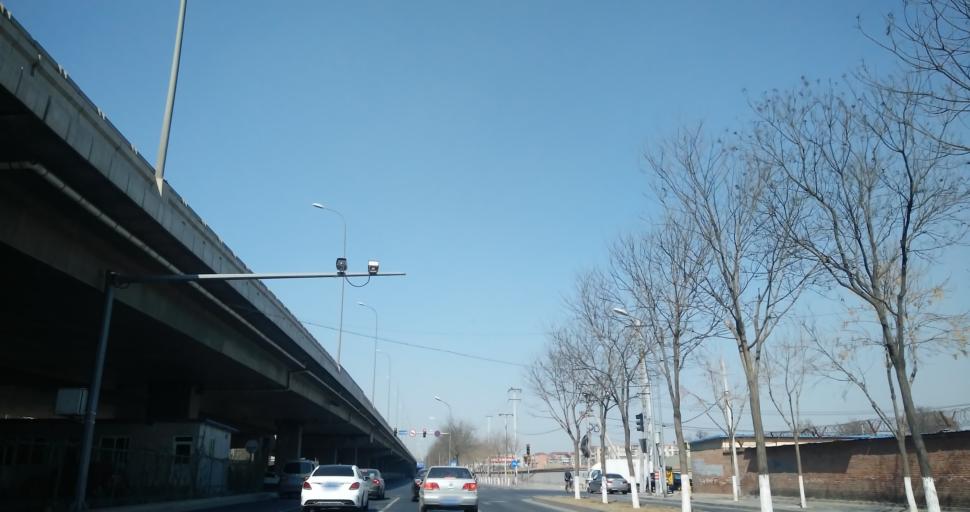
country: CN
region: Beijing
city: Jiugong
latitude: 39.7971
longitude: 116.4239
